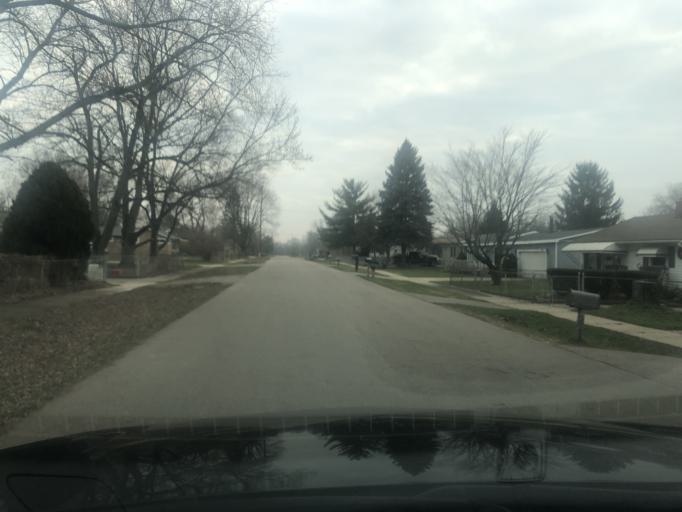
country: US
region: Michigan
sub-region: Wayne County
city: Belleville
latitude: 42.2169
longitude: -83.5506
